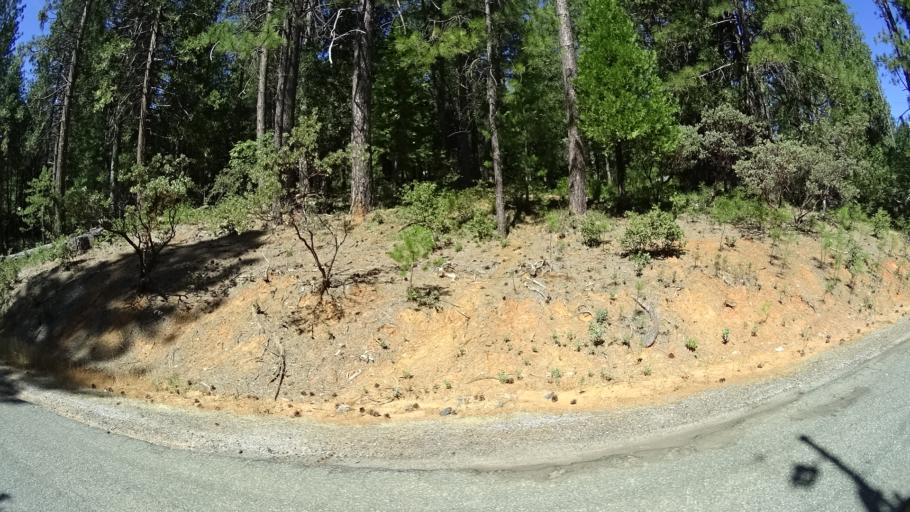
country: US
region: California
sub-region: Amador County
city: Pioneer
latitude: 38.4068
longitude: -120.5059
